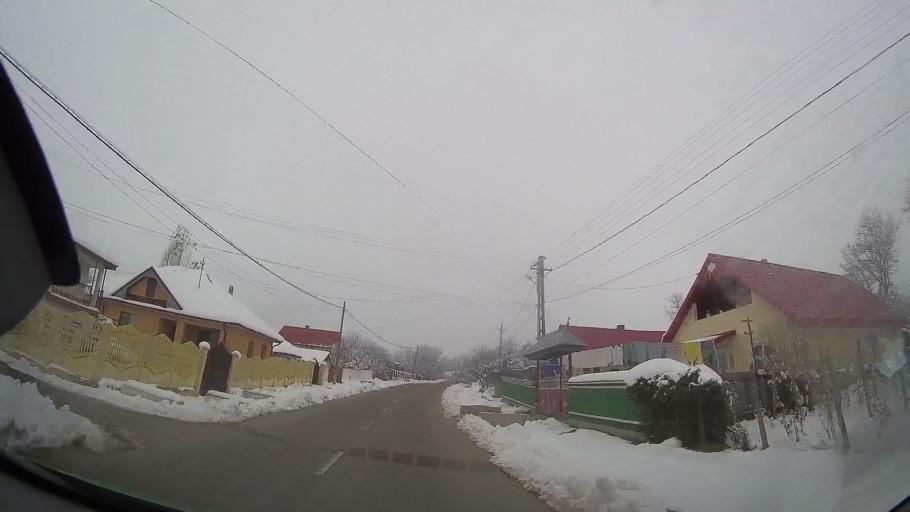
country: RO
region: Neamt
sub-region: Comuna Bozieni
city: Bozieni
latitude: 46.8369
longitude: 27.1546
